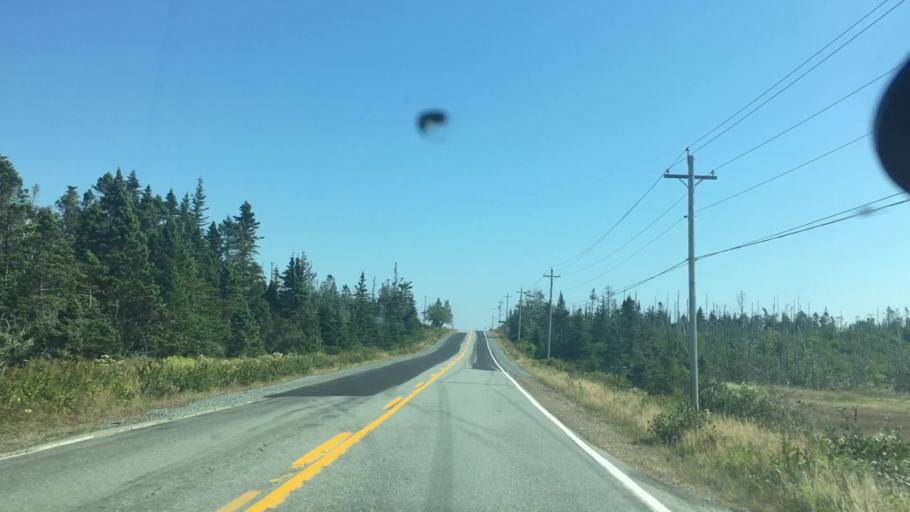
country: CA
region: Nova Scotia
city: New Glasgow
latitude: 44.9163
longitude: -62.3127
